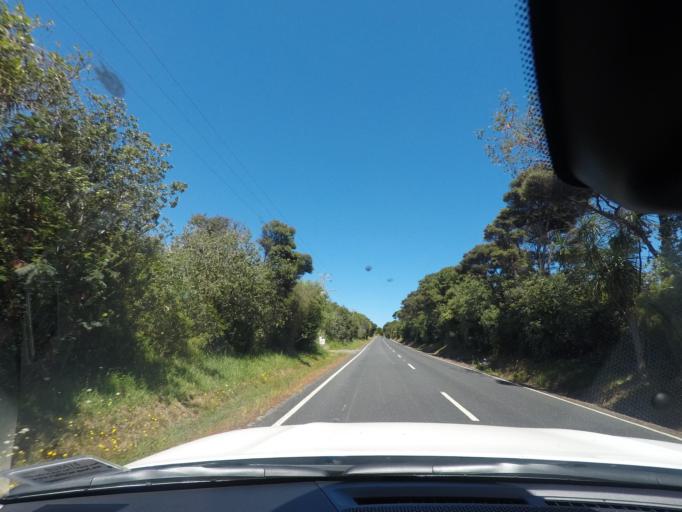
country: NZ
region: Auckland
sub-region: Auckland
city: Parakai
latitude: -36.5716
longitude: 174.3711
